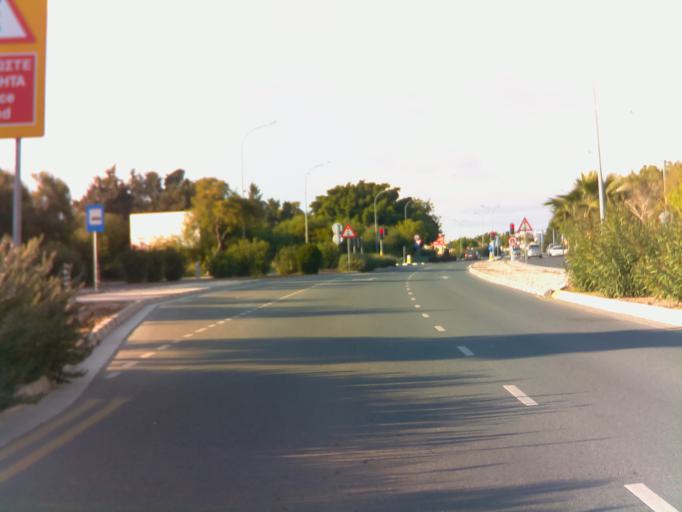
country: CY
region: Pafos
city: Paphos
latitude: 34.7551
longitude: 32.4252
